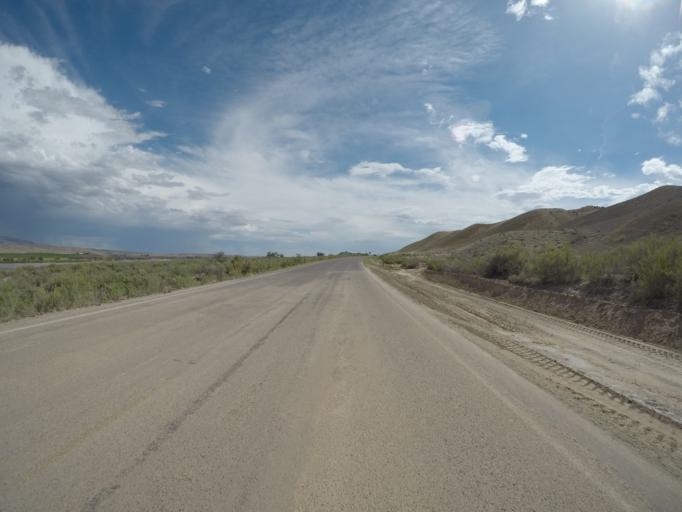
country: US
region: Utah
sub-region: Uintah County
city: Naples
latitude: 40.4321
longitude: -109.3314
